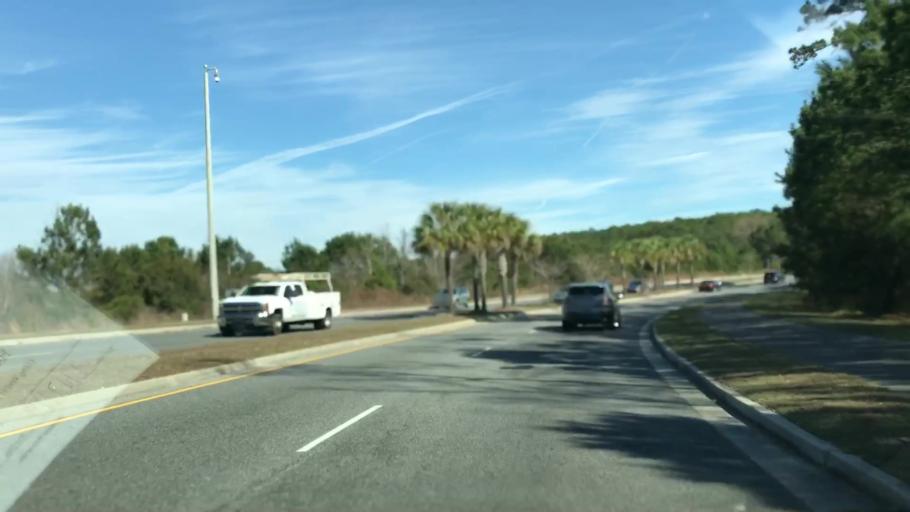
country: US
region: South Carolina
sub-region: Beaufort County
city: Bluffton
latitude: 32.2647
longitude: -80.8841
